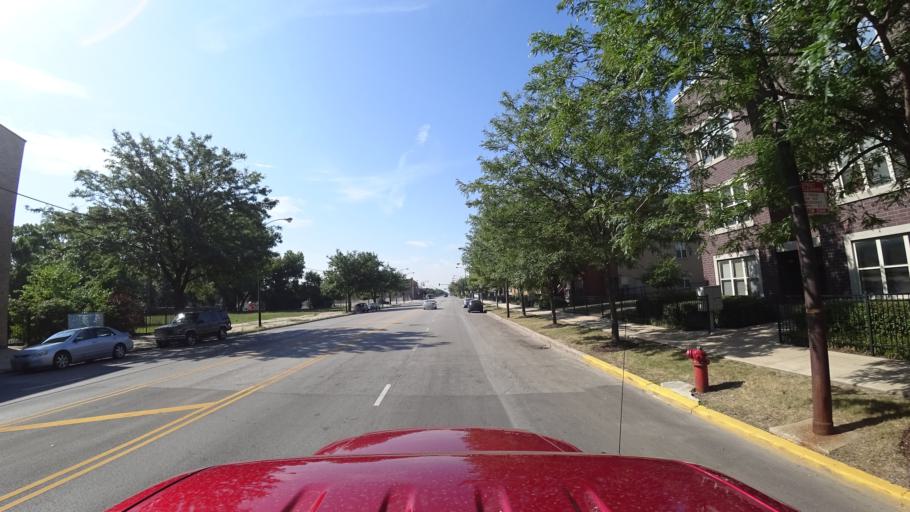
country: US
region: Illinois
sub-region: Cook County
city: Chicago
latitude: 41.8214
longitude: -87.6265
